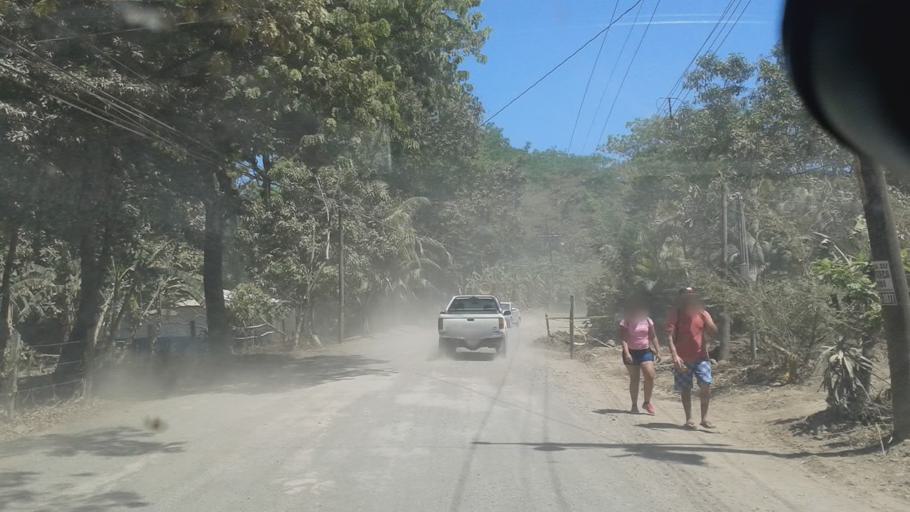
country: CR
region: Guanacaste
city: Samara
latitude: 9.9384
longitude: -85.6493
